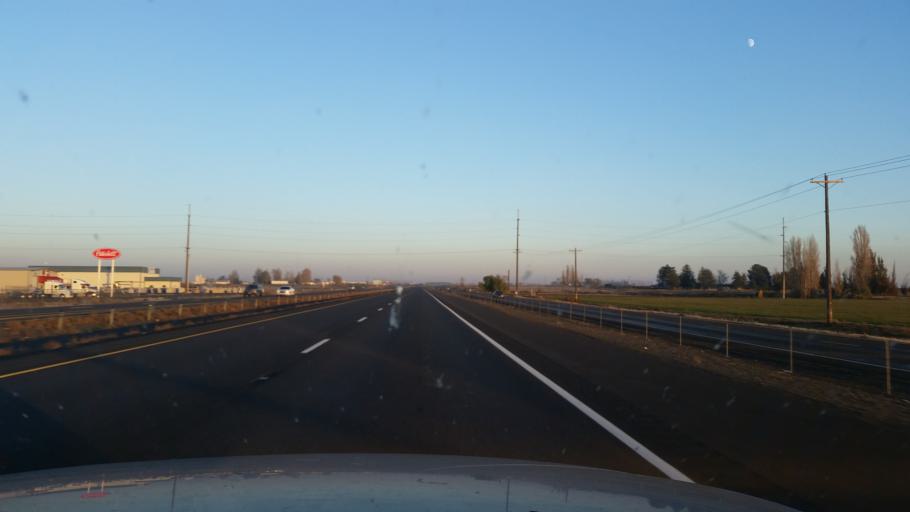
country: US
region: Washington
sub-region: Grant County
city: Moses Lake
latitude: 47.0965
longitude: -119.2186
